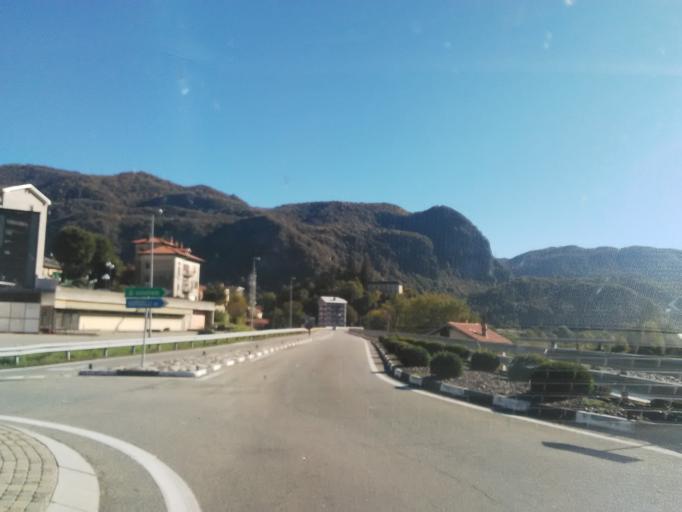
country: IT
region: Piedmont
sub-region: Provincia di Vercelli
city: Varallo
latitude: 45.8130
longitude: 8.2539
